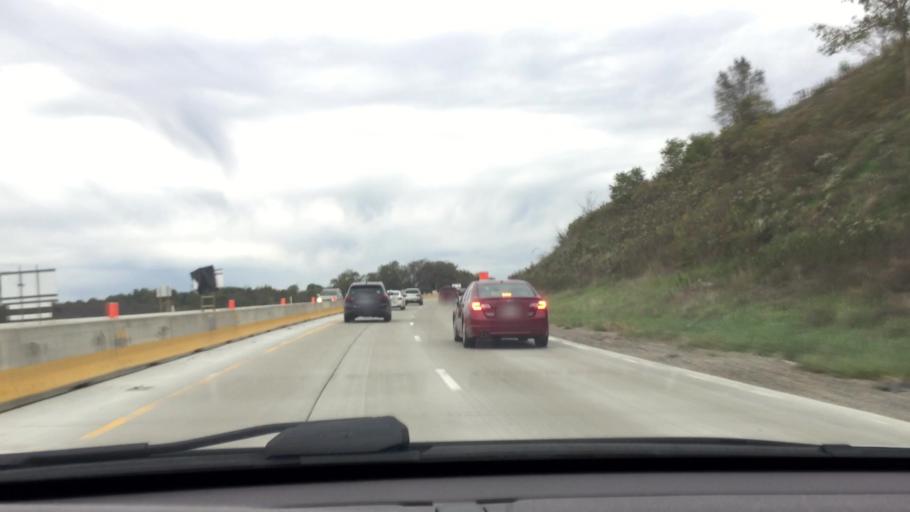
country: US
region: Pennsylvania
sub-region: Allegheny County
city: Enlow
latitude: 40.4690
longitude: -80.2442
